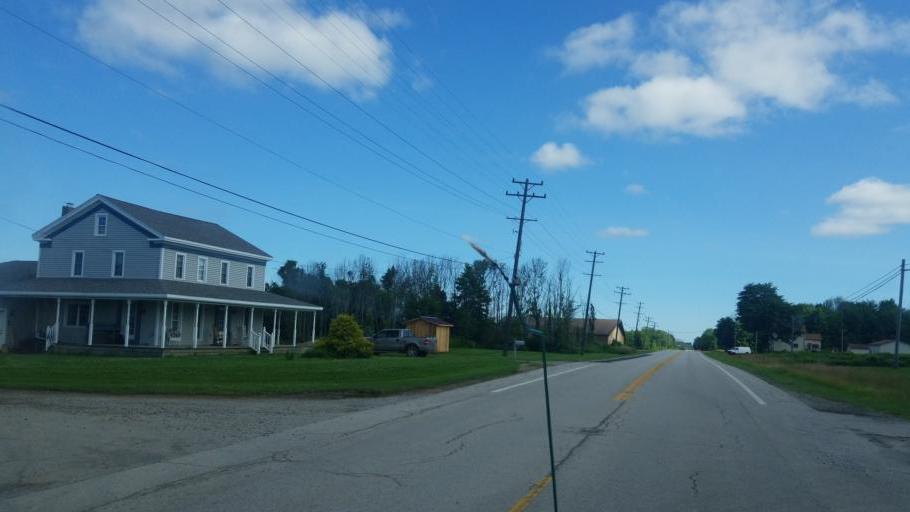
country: US
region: Ohio
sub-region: Ashtabula County
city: Conneaut
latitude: 41.8701
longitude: -80.5724
